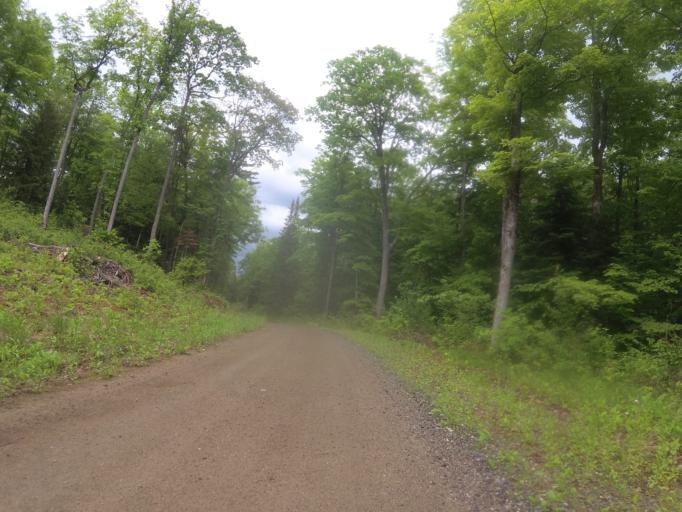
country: CA
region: Ontario
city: Renfrew
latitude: 45.1219
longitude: -76.8209
